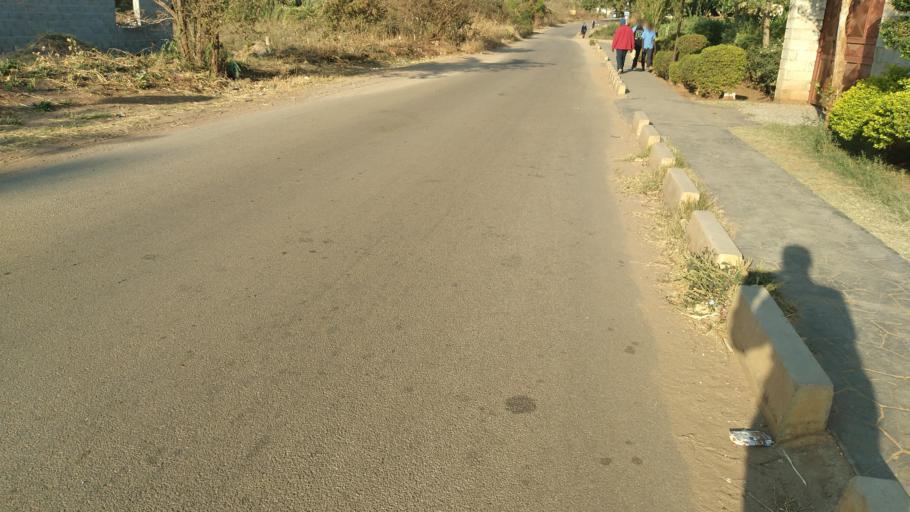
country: ZM
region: Lusaka
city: Lusaka
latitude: -15.5468
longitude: 28.2752
